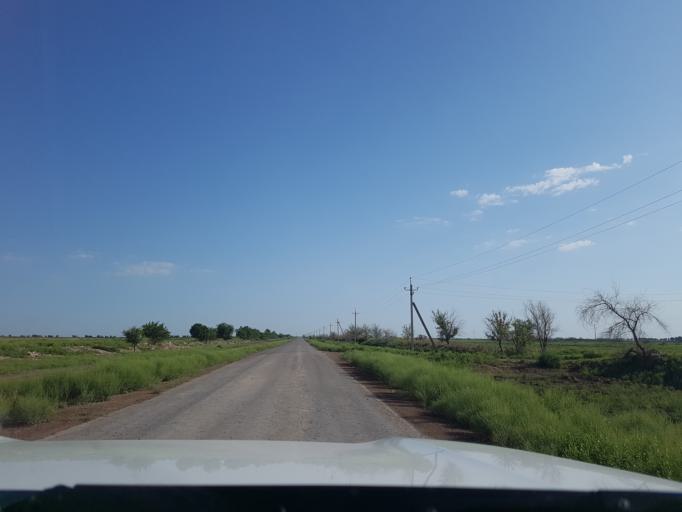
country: TM
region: Dasoguz
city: Koeneuergench
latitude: 41.8488
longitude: 58.7048
